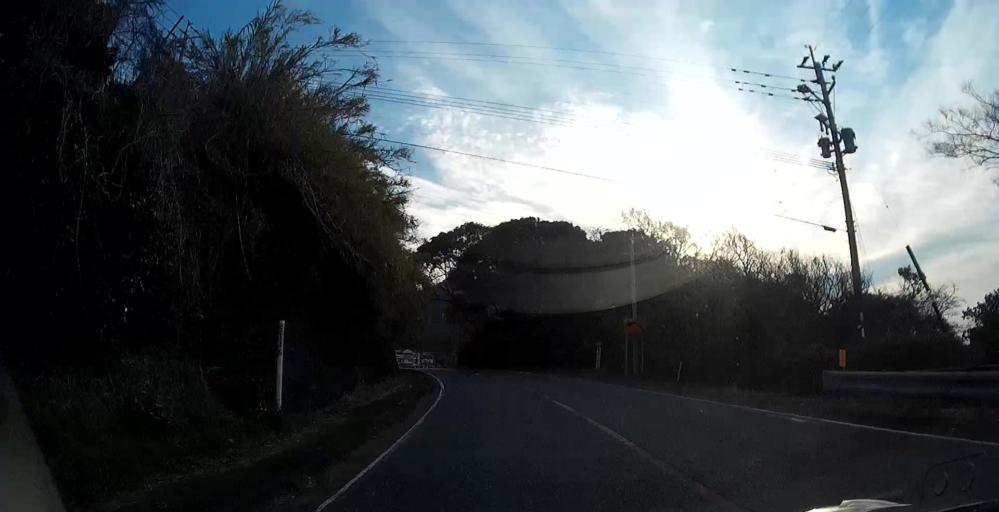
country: JP
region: Nagasaki
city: Shimabara
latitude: 32.6417
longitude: 130.4790
